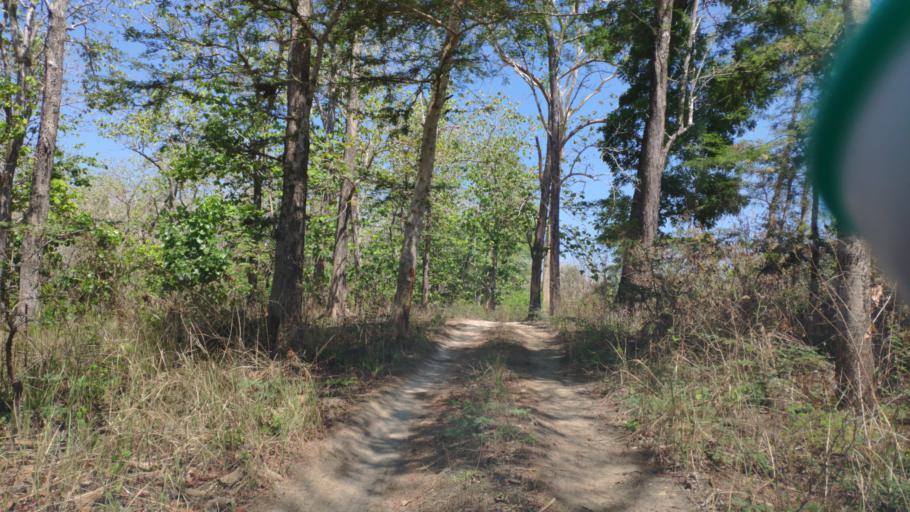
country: ID
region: Central Java
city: Suruhan
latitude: -7.0070
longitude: 111.5443
